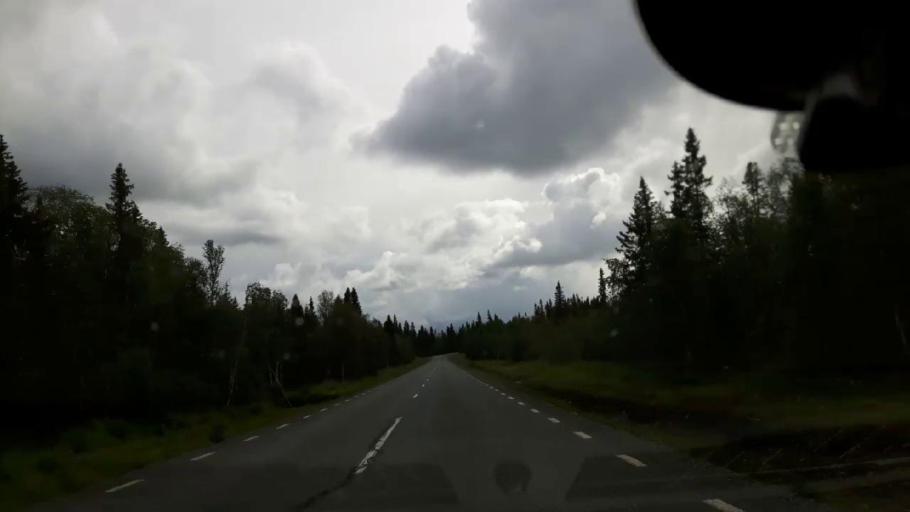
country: SE
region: Jaemtland
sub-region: Krokoms Kommun
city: Valla
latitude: 63.4499
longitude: 13.8281
